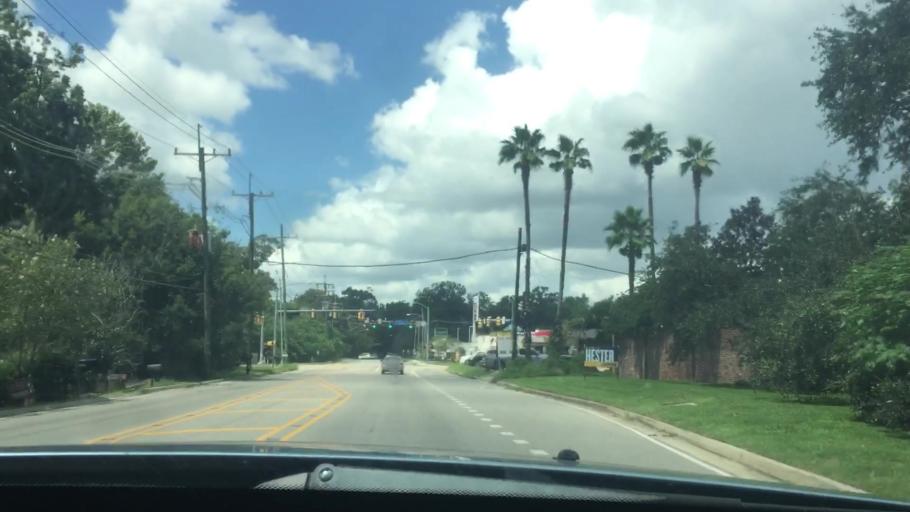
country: US
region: Louisiana
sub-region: East Baton Rouge Parish
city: Gardere
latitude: 30.3674
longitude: -91.1208
